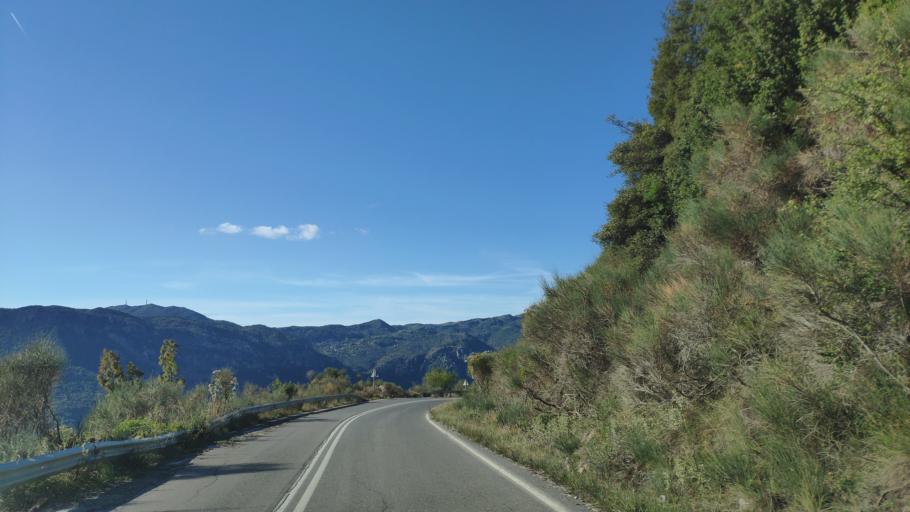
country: GR
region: Peloponnese
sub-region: Nomos Arkadias
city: Dimitsana
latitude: 37.5637
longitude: 22.0628
